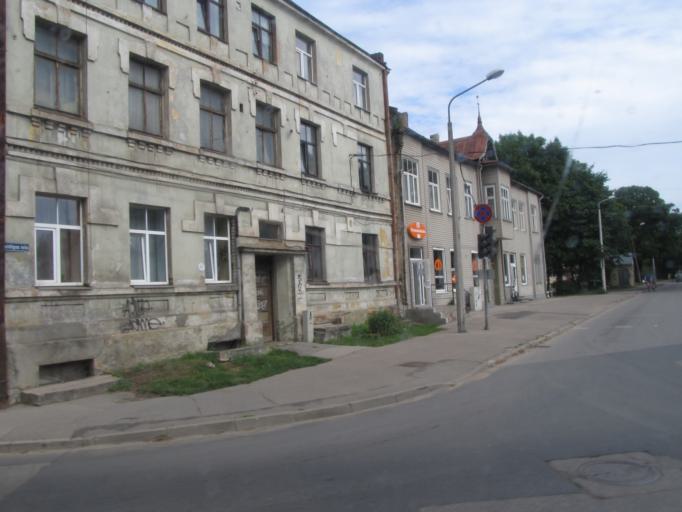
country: LV
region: Riga
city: Riga
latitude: 56.9508
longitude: 24.0651
